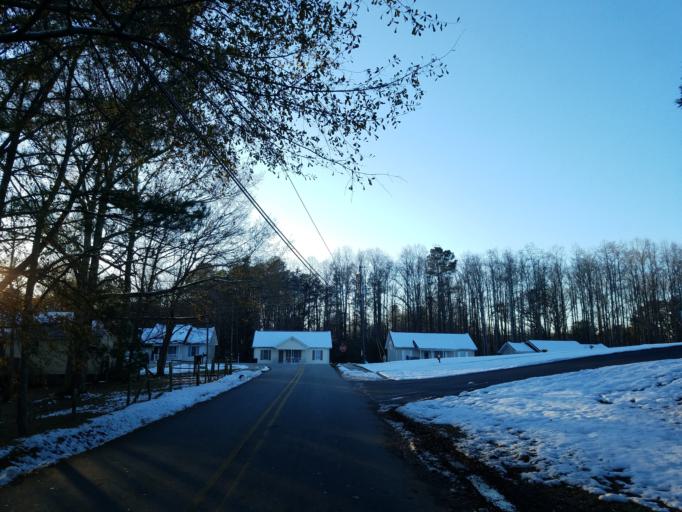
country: US
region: Georgia
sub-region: Dawson County
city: Dawsonville
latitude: 34.4188
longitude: -84.1218
